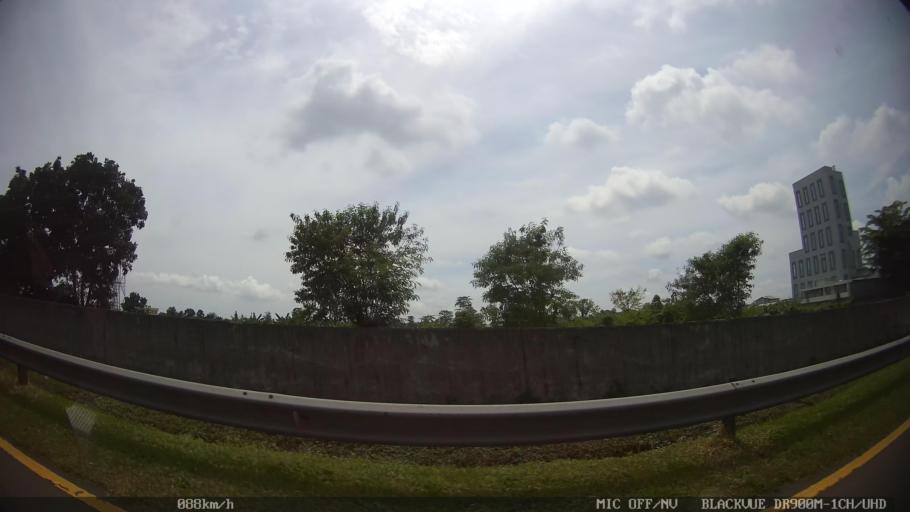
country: ID
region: North Sumatra
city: Labuhan Deli
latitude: 3.6862
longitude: 98.6817
